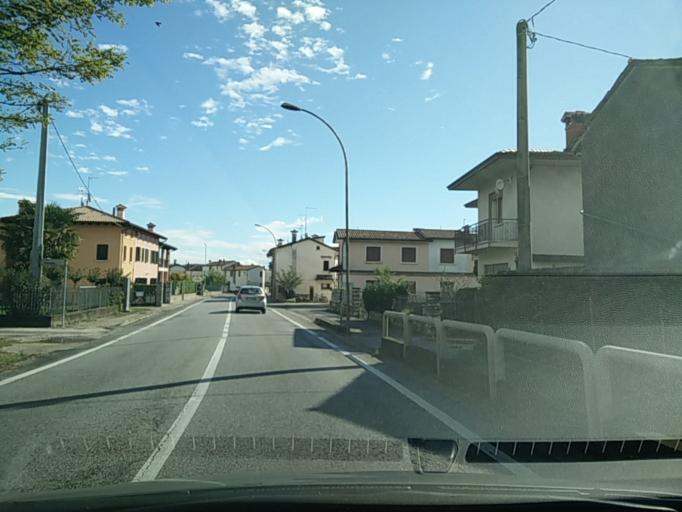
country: IT
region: Veneto
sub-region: Provincia di Treviso
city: Bigolino
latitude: 45.8705
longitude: 12.0077
